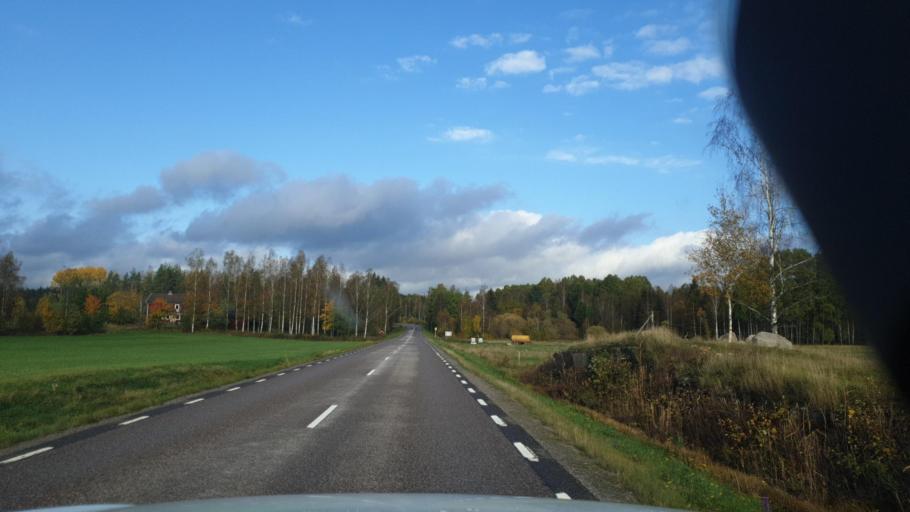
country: SE
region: Vaermland
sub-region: Arvika Kommun
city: Arvika
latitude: 59.5002
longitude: 12.6833
